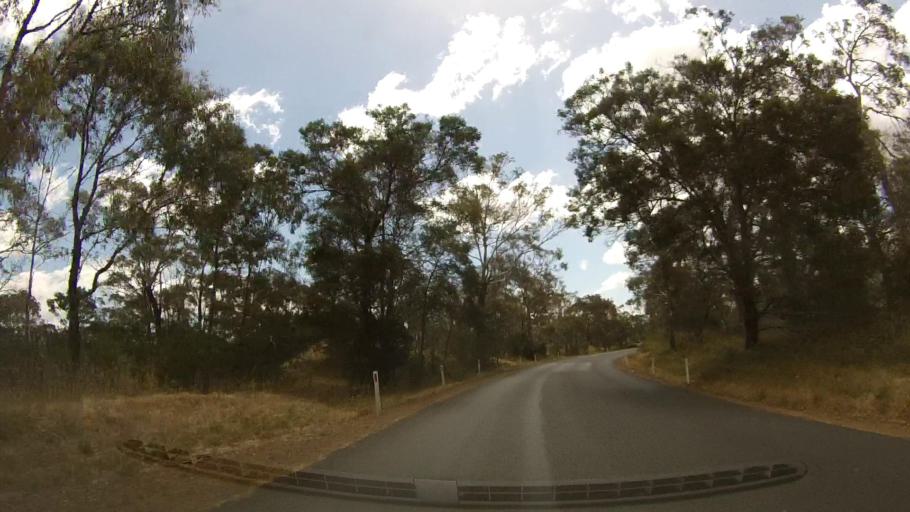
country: AU
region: Tasmania
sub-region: Clarence
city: Seven Mile Beach
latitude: -42.8283
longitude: 147.5090
